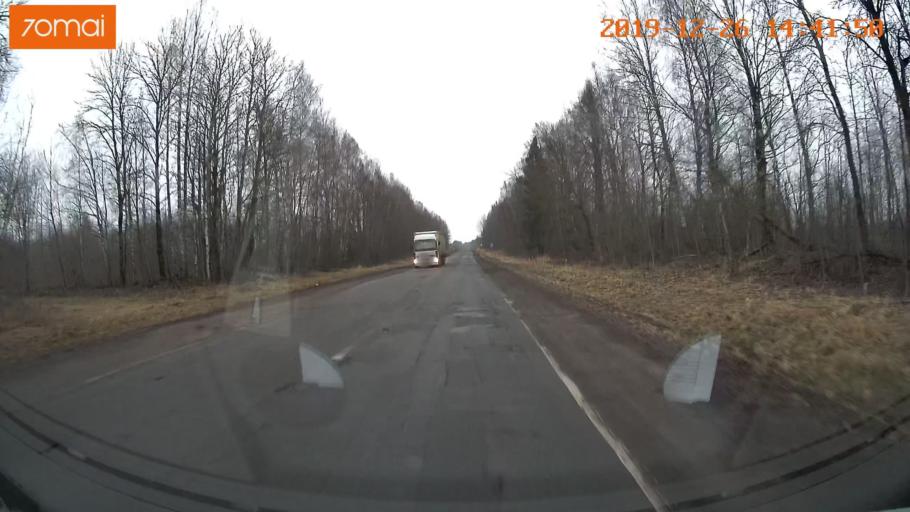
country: RU
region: Jaroslavl
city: Poshekhon'ye
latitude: 58.3681
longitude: 39.0240
